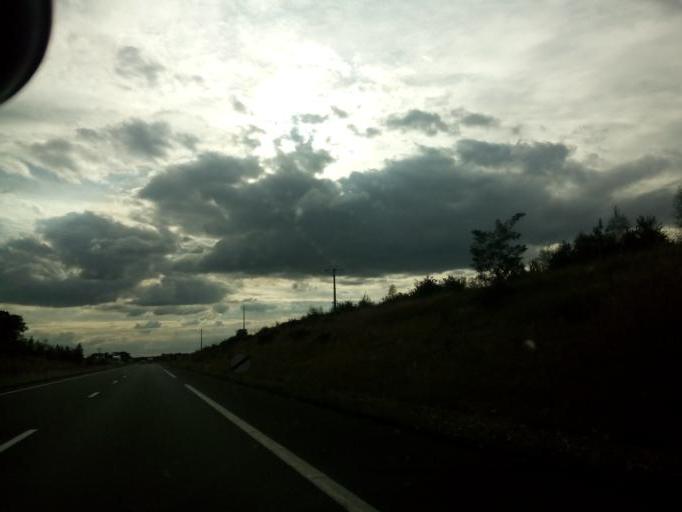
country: FR
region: Centre
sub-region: Departement du Loir-et-Cher
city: Saint-Georges-sur-Cher
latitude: 47.2921
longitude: 1.0971
